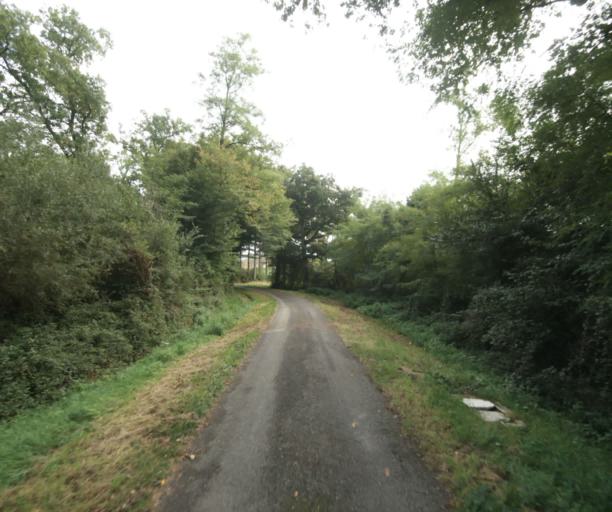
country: FR
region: Aquitaine
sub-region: Departement des Landes
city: Villeneuve-de-Marsan
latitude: 43.9077
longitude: -0.2311
